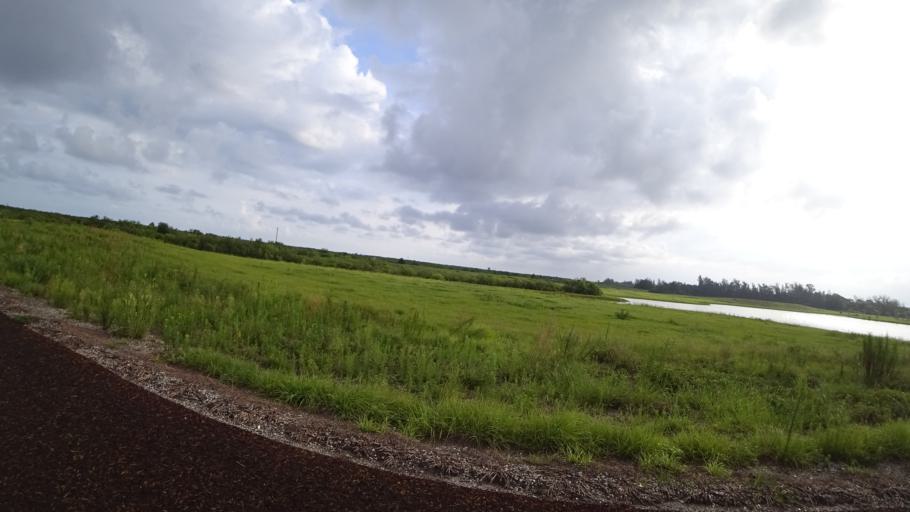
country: US
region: Florida
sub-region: Manatee County
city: Holmes Beach
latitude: 27.5098
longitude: -82.6701
